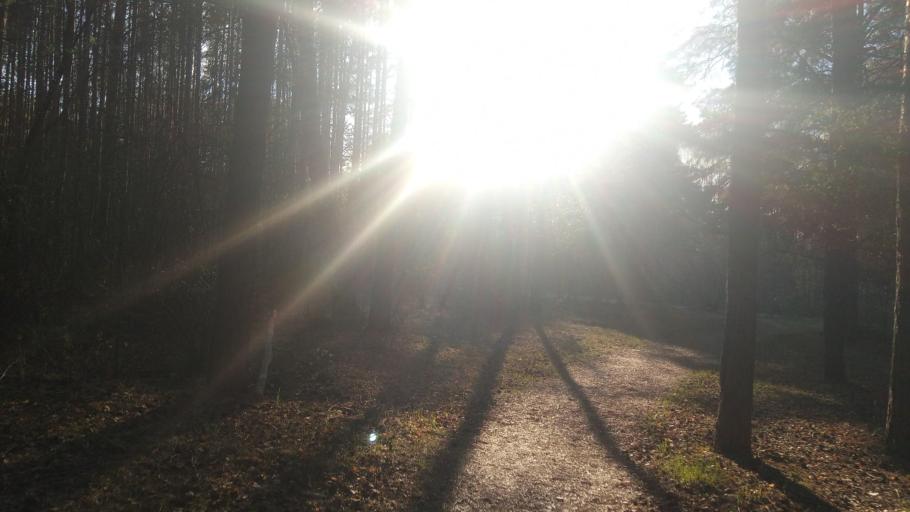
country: RU
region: Chelyabinsk
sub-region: Gorod Chelyabinsk
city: Chelyabinsk
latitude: 55.1487
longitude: 61.3318
